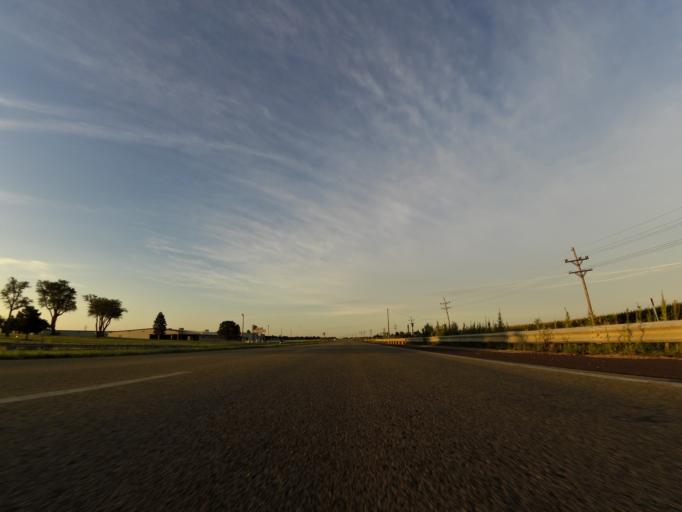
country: US
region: Kansas
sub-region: Reno County
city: South Hutchinson
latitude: 38.0044
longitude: -97.9405
